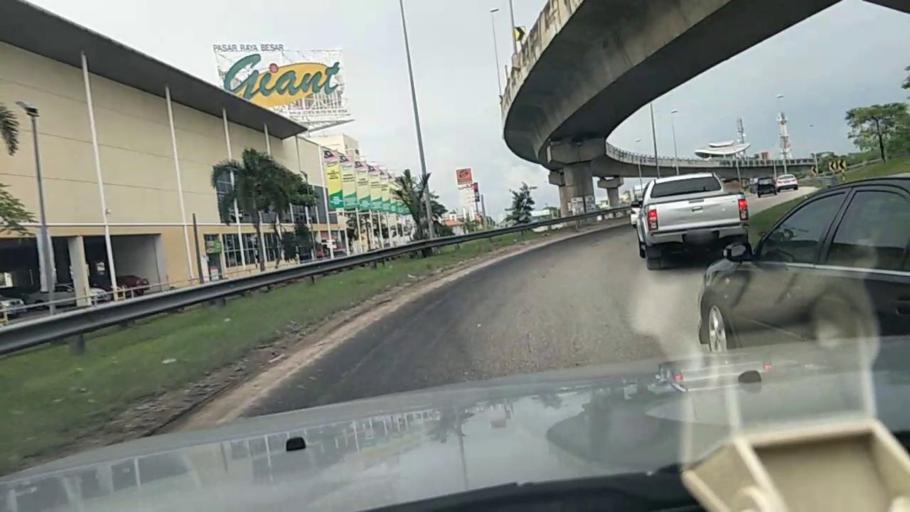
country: MY
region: Selangor
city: Klang
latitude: 3.1071
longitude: 101.4419
